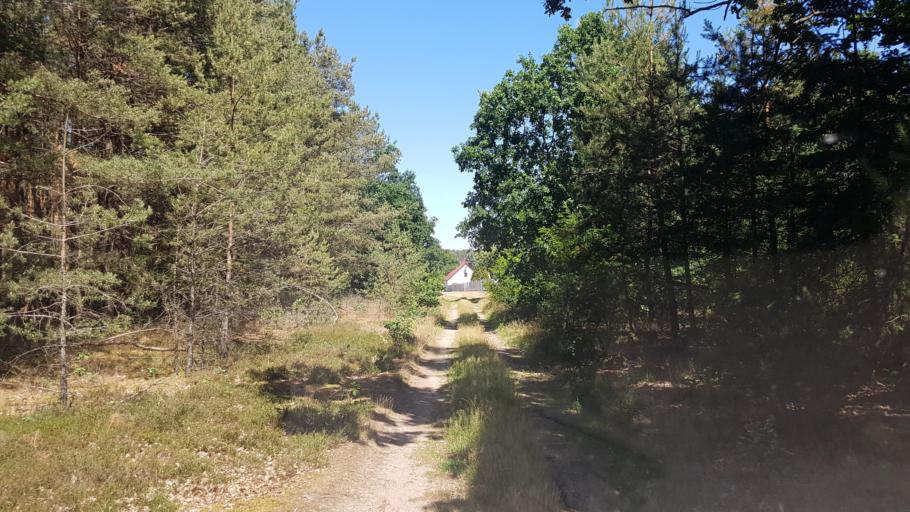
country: DE
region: Brandenburg
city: Treuenbrietzen
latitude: 52.0361
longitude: 12.8652
